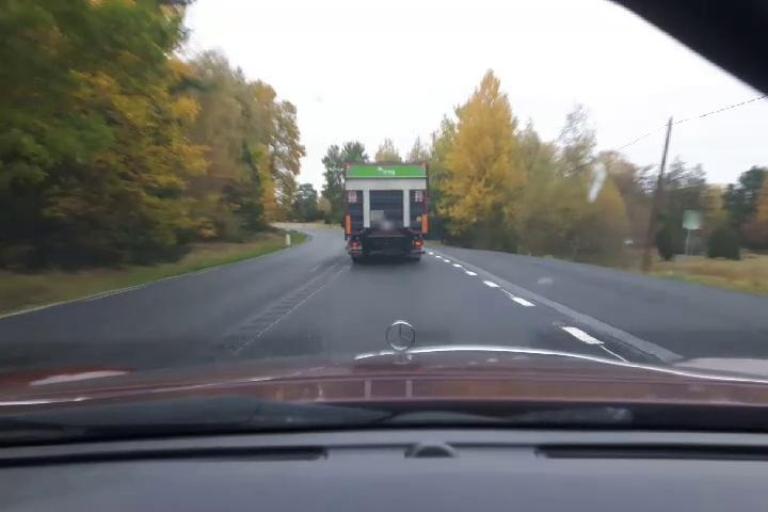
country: SE
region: Soedermanland
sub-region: Strangnas Kommun
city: Strangnas
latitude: 59.4302
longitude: 17.0248
